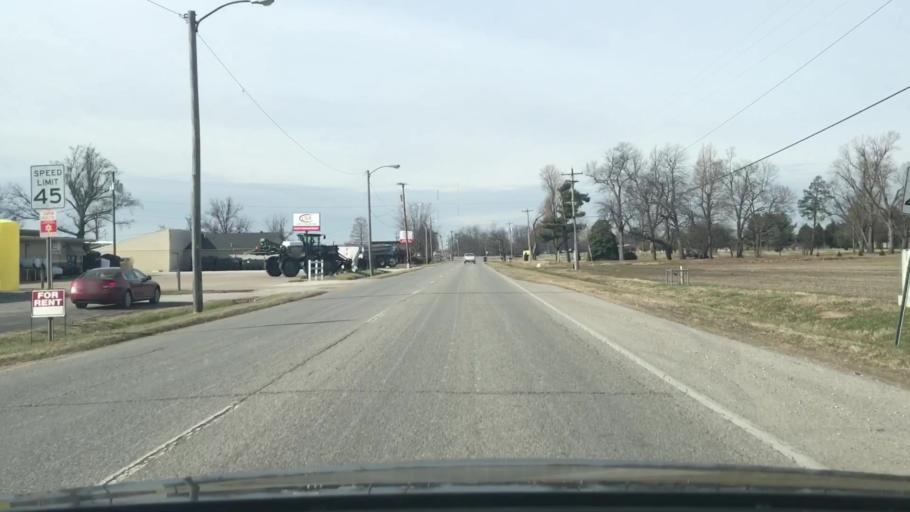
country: US
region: Kentucky
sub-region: Daviess County
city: Owensboro
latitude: 37.7736
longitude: -87.1426
